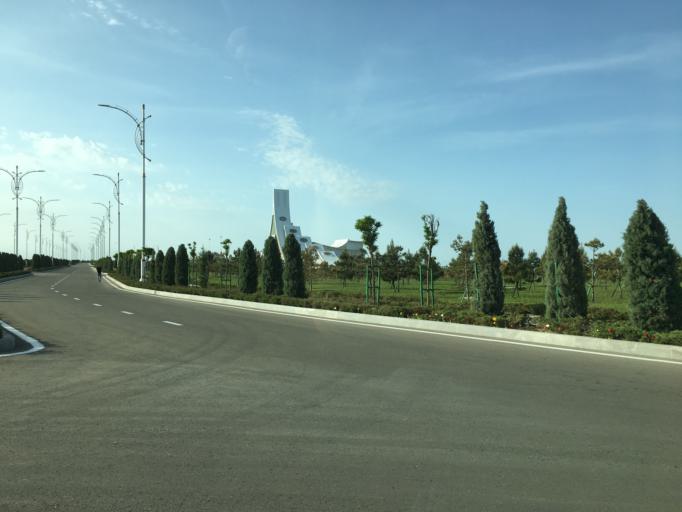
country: TM
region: Balkan
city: Turkmenbasy
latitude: 39.9466
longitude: 52.8846
